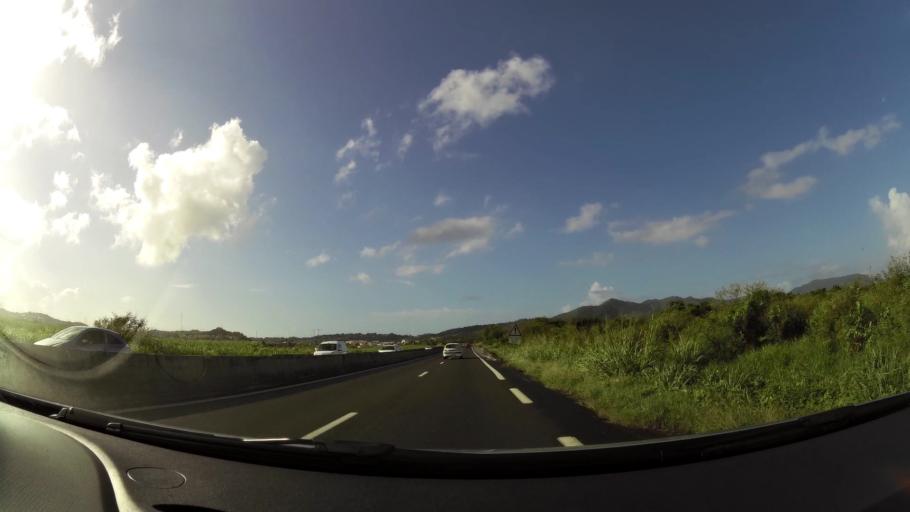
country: MQ
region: Martinique
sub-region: Martinique
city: Ducos
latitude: 14.5383
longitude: -60.9792
